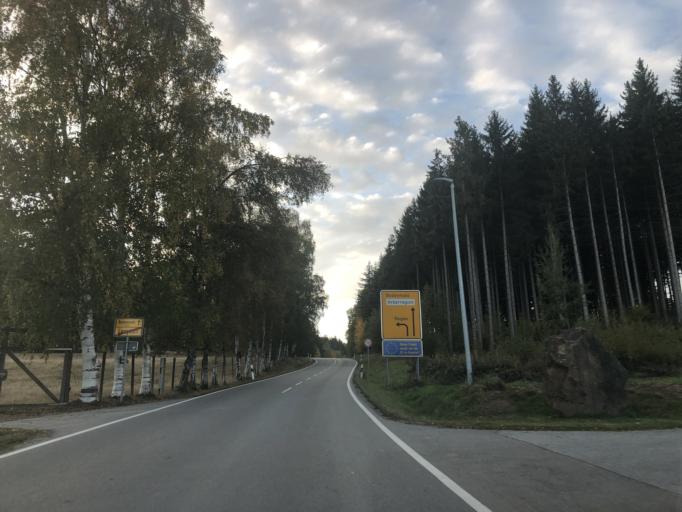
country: DE
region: Bavaria
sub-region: Lower Bavaria
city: Langdorf
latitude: 49.0158
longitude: 13.1454
